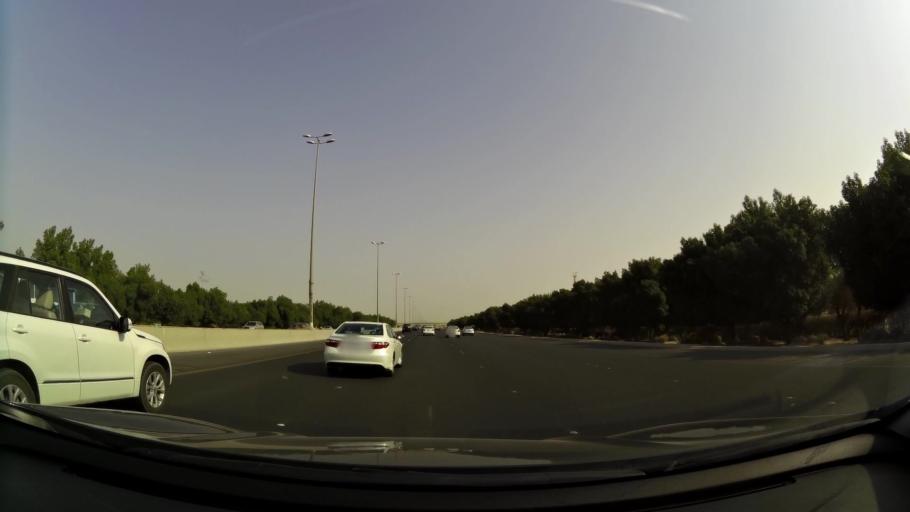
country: KW
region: Muhafazat al Jahra'
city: Al Jahra'
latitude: 29.3336
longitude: 47.7287
